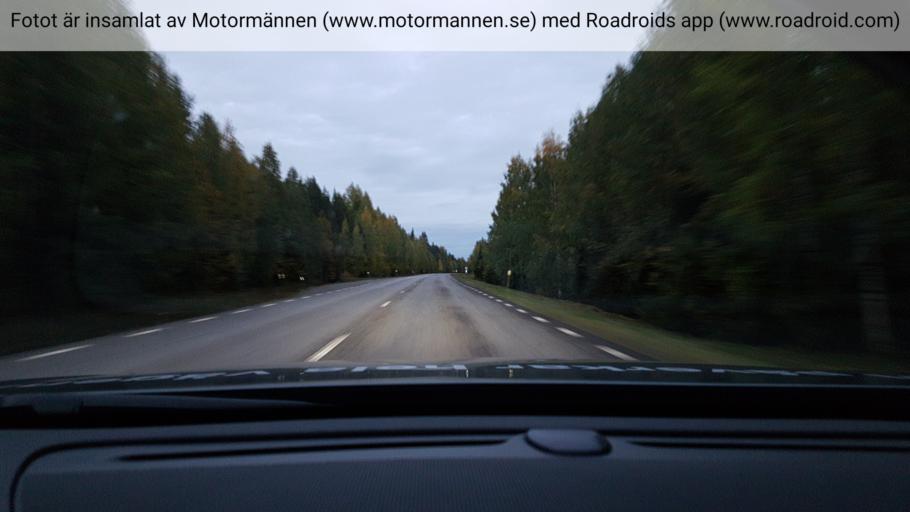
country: SE
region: Norrbotten
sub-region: Alvsbyns Kommun
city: AElvsbyn
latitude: 65.7799
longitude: 20.8258
